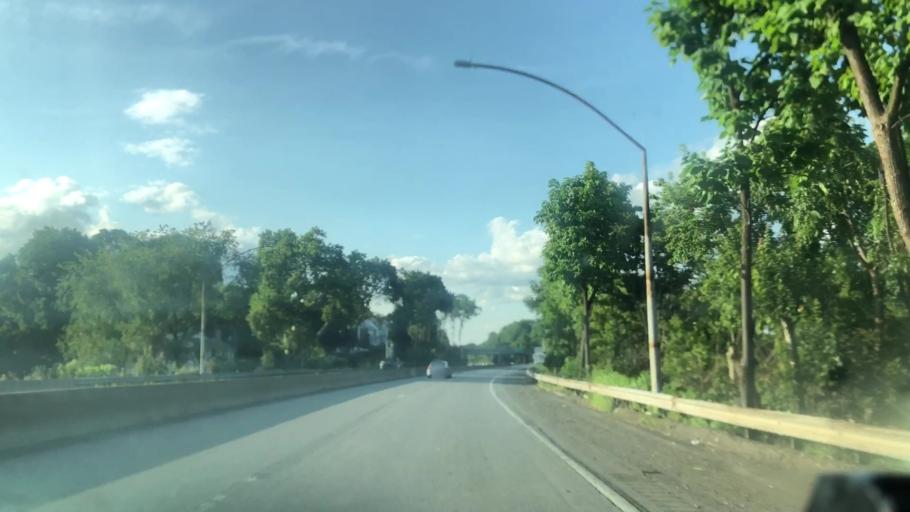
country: US
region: Pennsylvania
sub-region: Northampton County
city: Bethlehem
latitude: 40.6187
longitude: -75.3851
